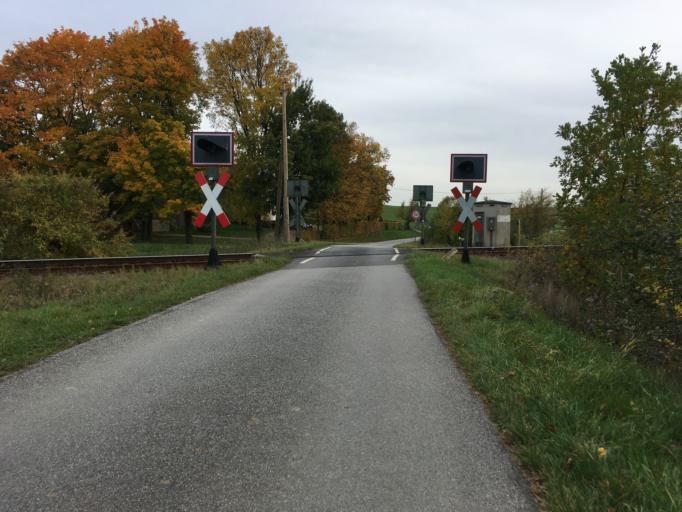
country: DE
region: Baden-Wuerttemberg
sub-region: Karlsruhe Region
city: Buchen
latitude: 49.5071
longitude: 9.3292
